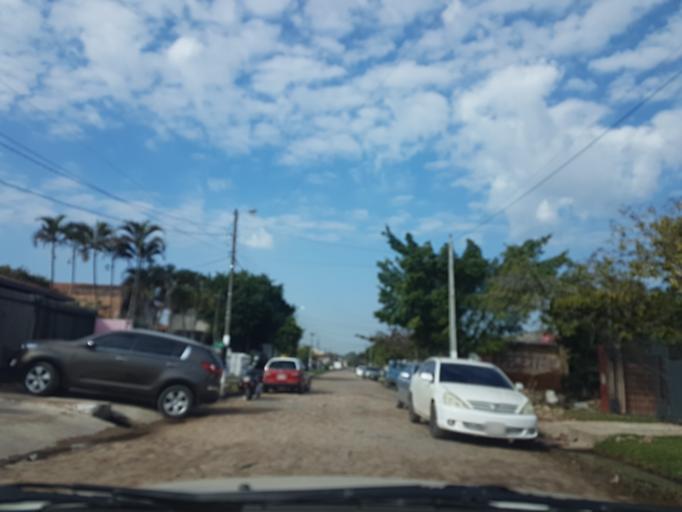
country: PY
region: Central
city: Colonia Mariano Roque Alonso
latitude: -25.2101
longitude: -57.5363
